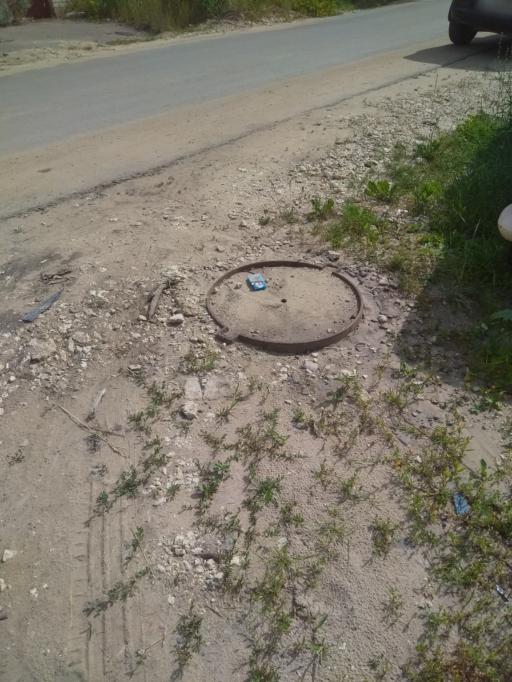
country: RU
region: Voronezj
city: Pridonskoy
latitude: 51.6446
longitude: 39.0920
